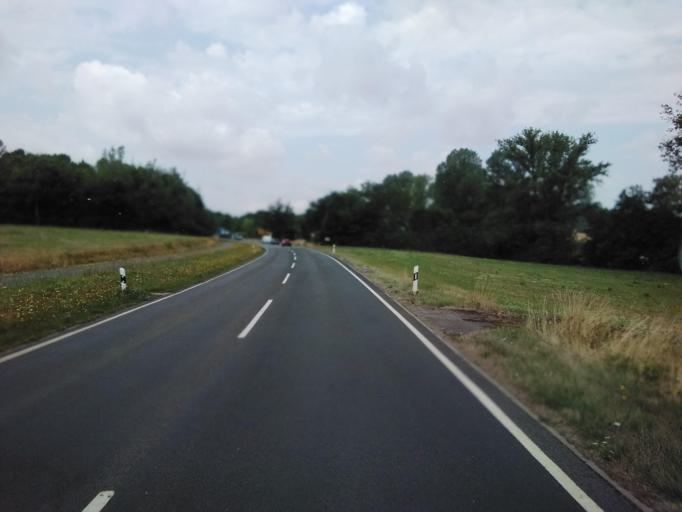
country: DE
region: Bavaria
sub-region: Regierungsbezirk Mittelfranken
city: Langenzenn
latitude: 49.4935
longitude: 10.7781
